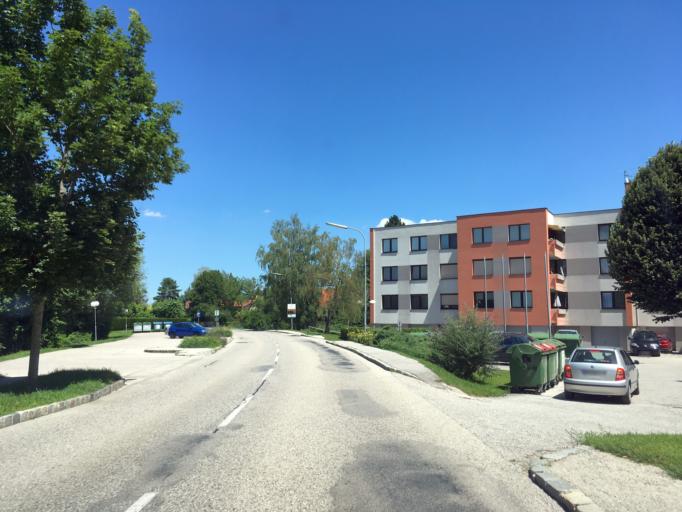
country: AT
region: Lower Austria
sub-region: Politischer Bezirk Wiener Neustadt
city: Bad Erlach
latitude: 47.7218
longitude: 16.2094
